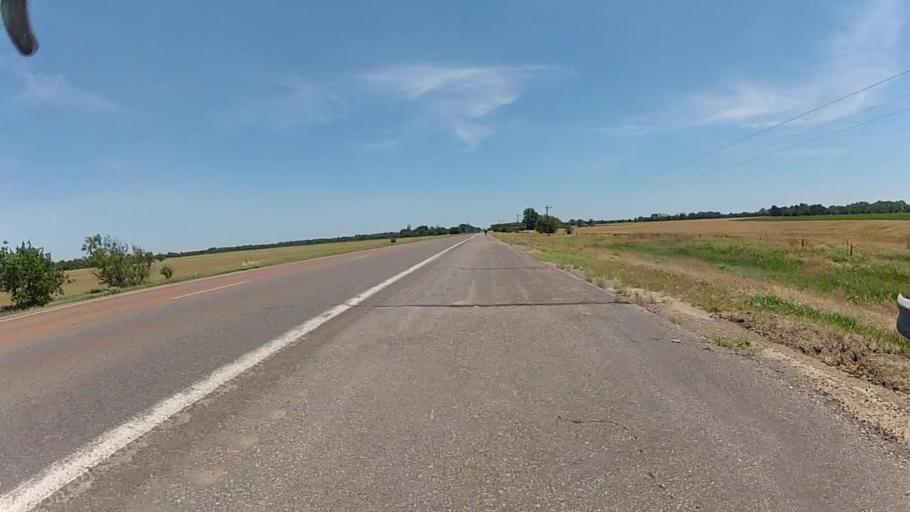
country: US
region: Kansas
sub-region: Barber County
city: Medicine Lodge
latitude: 37.2537
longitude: -98.3453
